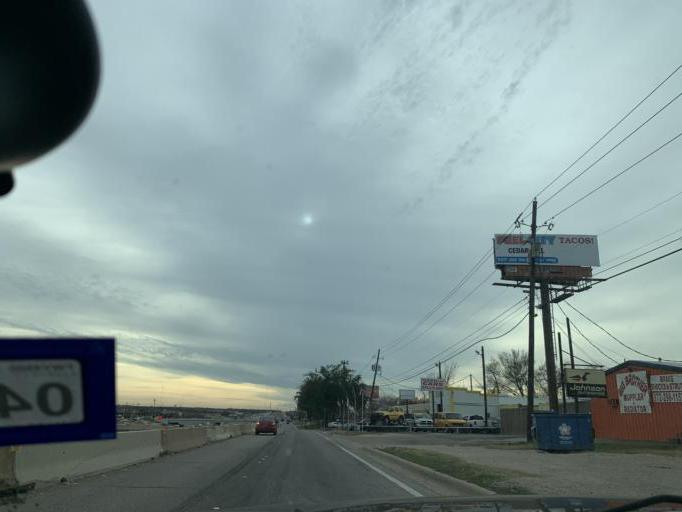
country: US
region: Texas
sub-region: Dallas County
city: Duncanville
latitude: 32.6363
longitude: -96.8975
